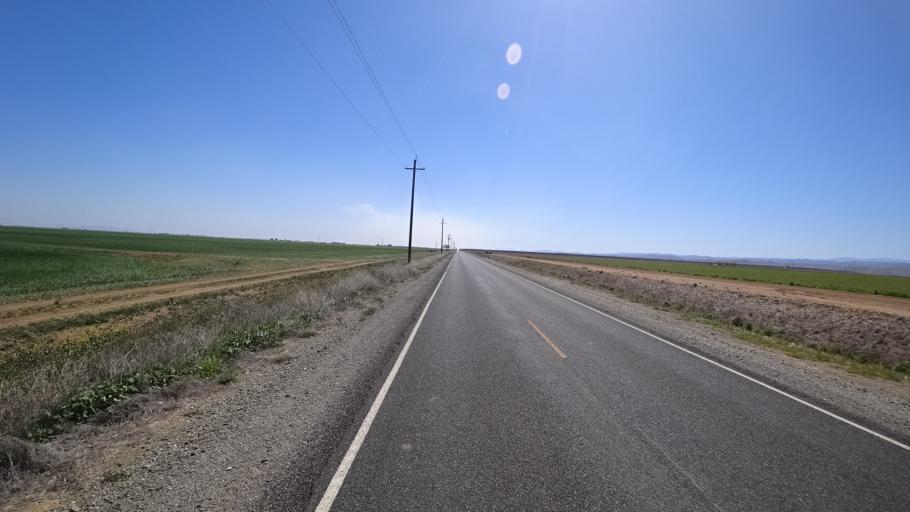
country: US
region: California
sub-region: Glenn County
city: Willows
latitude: 39.4902
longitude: -122.2491
